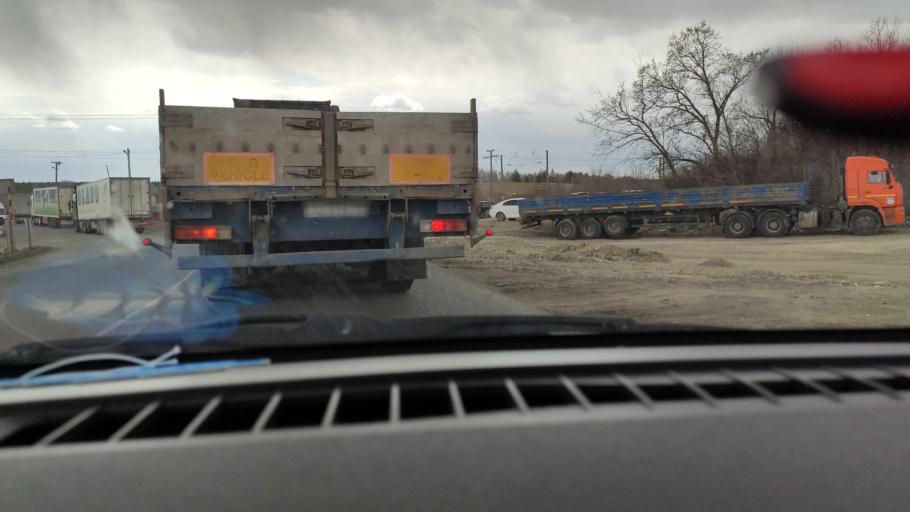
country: RU
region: Saratov
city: Sinodskoye
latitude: 52.0104
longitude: 46.6880
